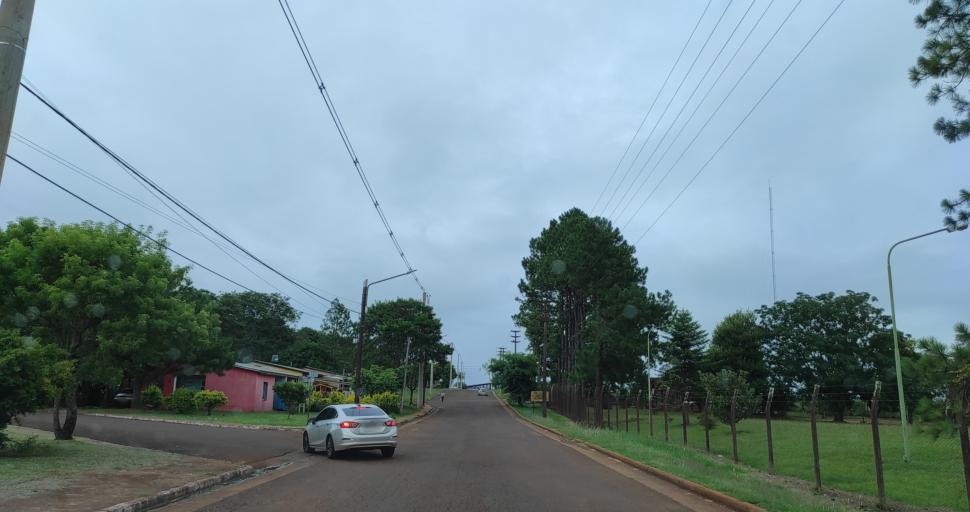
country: AR
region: Misiones
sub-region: Departamento de Apostoles
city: San Jose
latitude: -27.7660
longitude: -55.7756
